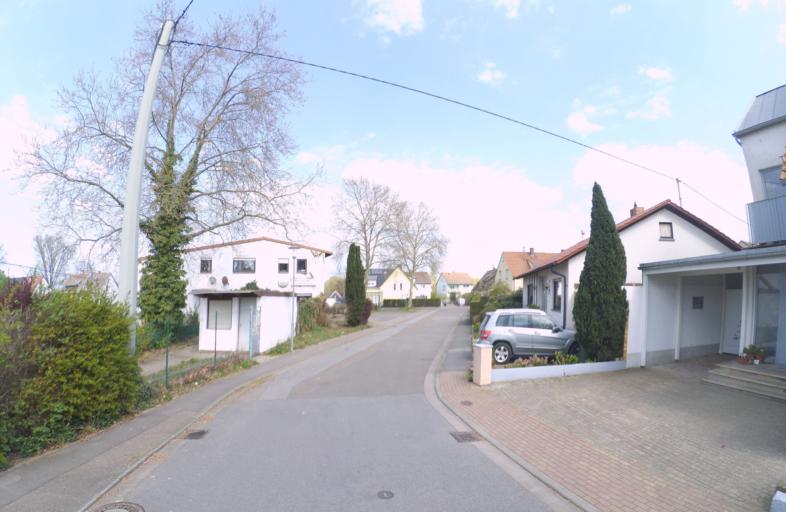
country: DE
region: Baden-Wuerttemberg
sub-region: Karlsruhe Region
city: Ladenburg
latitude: 49.4710
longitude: 8.5939
